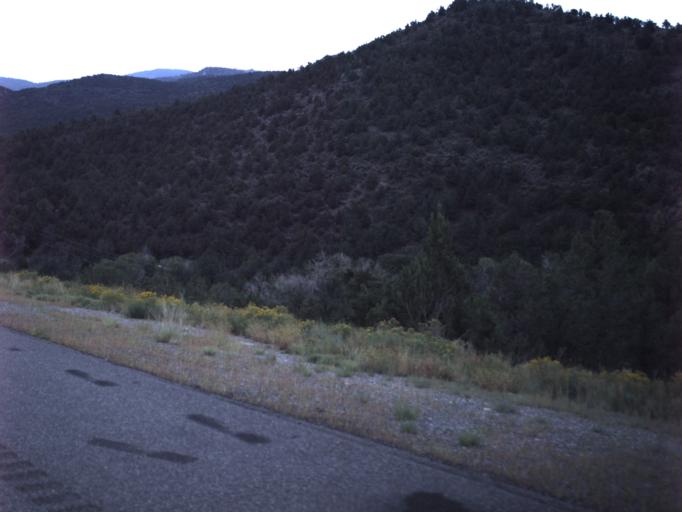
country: US
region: Utah
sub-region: Sevier County
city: Monroe
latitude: 38.5486
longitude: -112.3832
